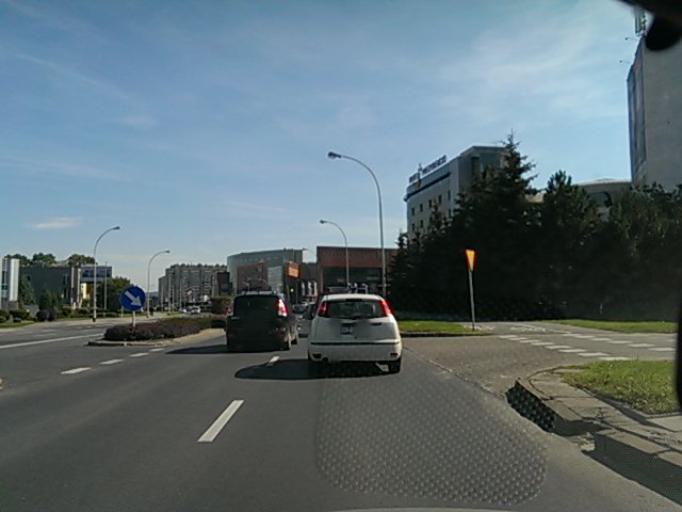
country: PL
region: Subcarpathian Voivodeship
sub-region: Rzeszow
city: Rzeszow
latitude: 50.0289
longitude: 22.0097
